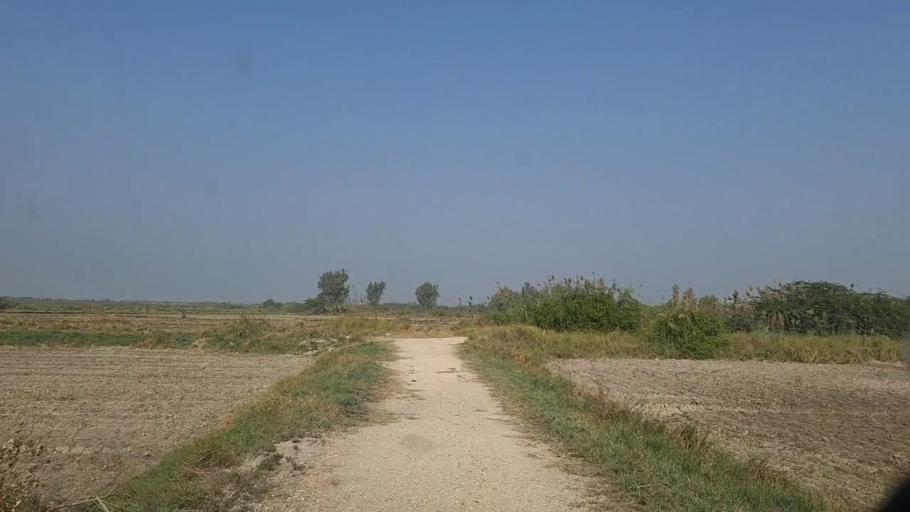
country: PK
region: Sindh
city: Thatta
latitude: 24.6563
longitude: 67.9174
